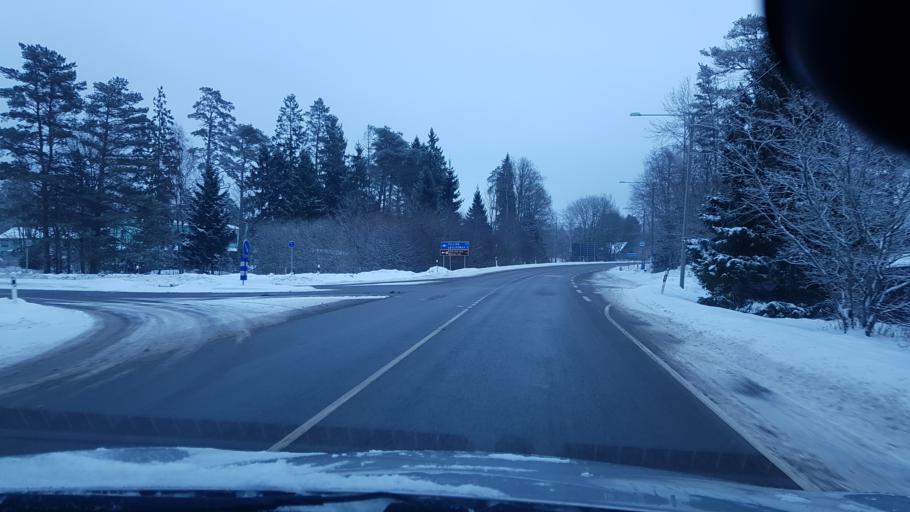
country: EE
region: Harju
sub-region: Keila linn
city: Keila
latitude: 59.3413
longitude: 24.2658
